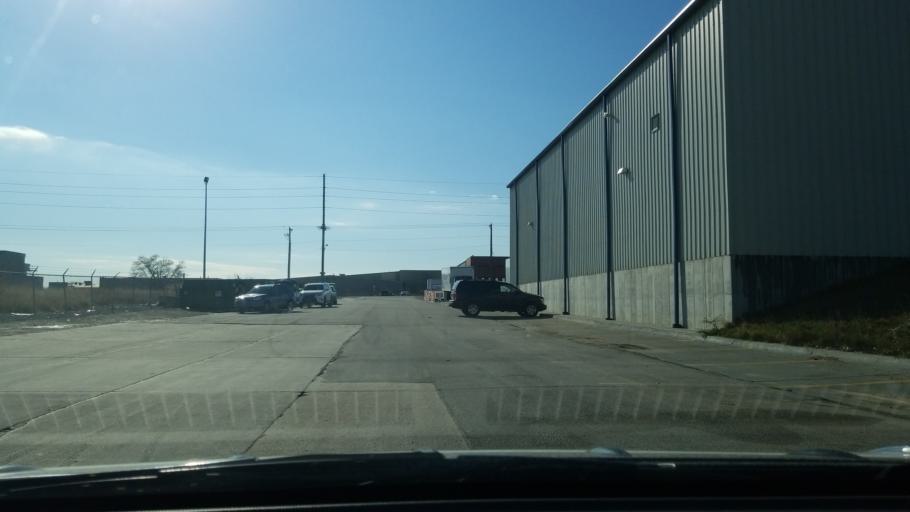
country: US
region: Nebraska
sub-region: Douglas County
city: Ralston
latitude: 41.2174
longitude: -96.0738
